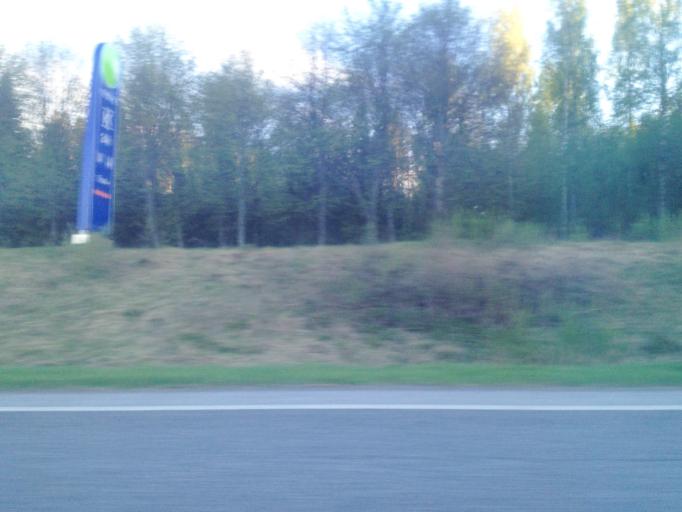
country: FI
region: Haeme
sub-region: Haemeenlinna
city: Janakkala
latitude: 60.8556
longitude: 24.5948
